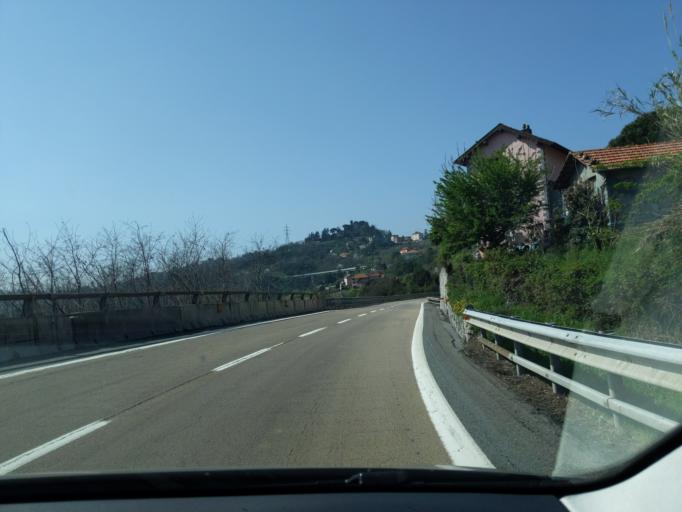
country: IT
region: Liguria
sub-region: Provincia di Genova
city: Pedemonte
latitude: 44.5015
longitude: 8.9218
